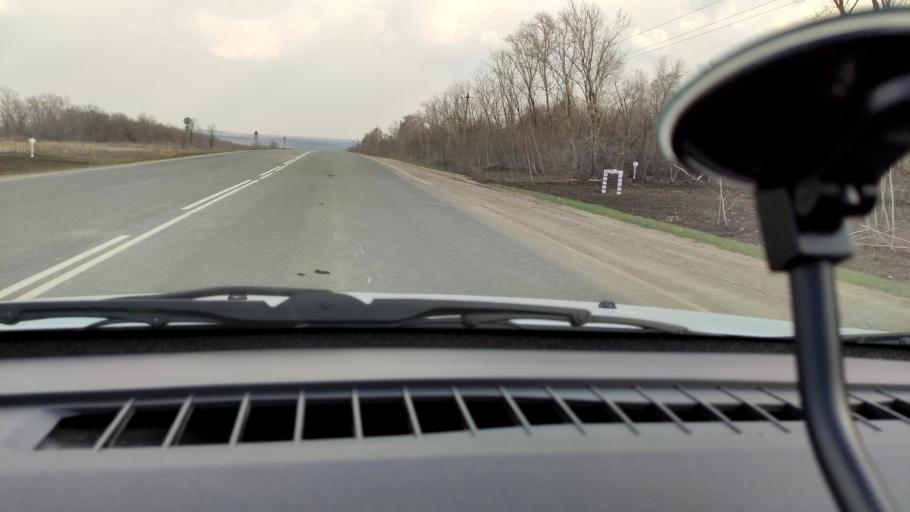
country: RU
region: Samara
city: Dubovyy Umet
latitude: 53.0794
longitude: 50.3497
